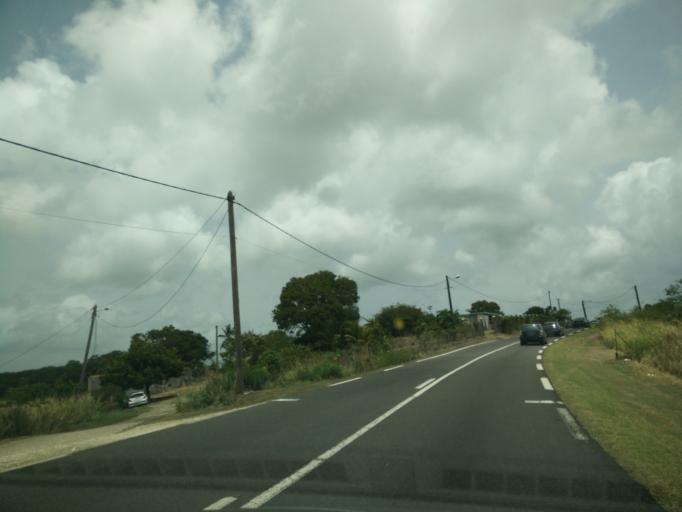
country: GP
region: Guadeloupe
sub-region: Guadeloupe
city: Petit-Canal
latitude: 16.3754
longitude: -61.4739
